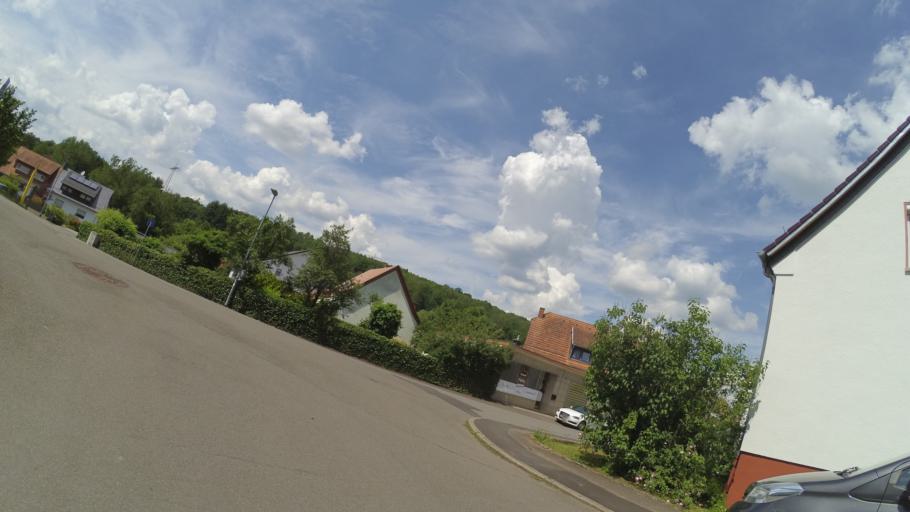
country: DE
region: Saarland
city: Homburg
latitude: 49.2993
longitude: 7.3644
